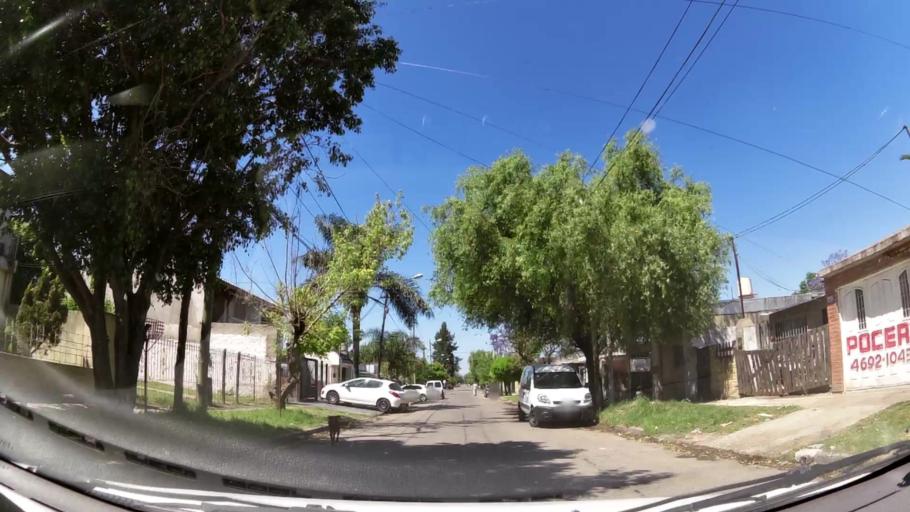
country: AR
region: Buenos Aires
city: Ituzaingo
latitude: -34.6849
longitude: -58.6574
